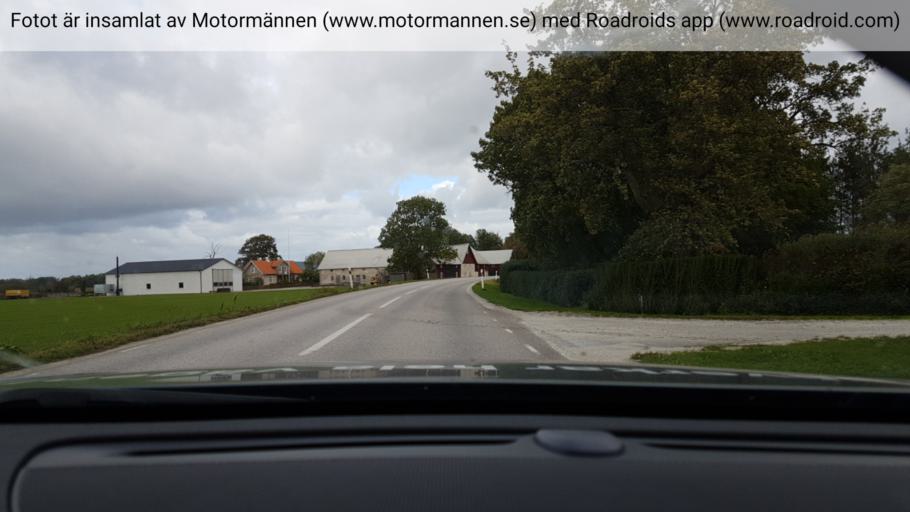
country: SE
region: Gotland
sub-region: Gotland
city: Vibble
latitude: 57.5064
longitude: 18.3714
